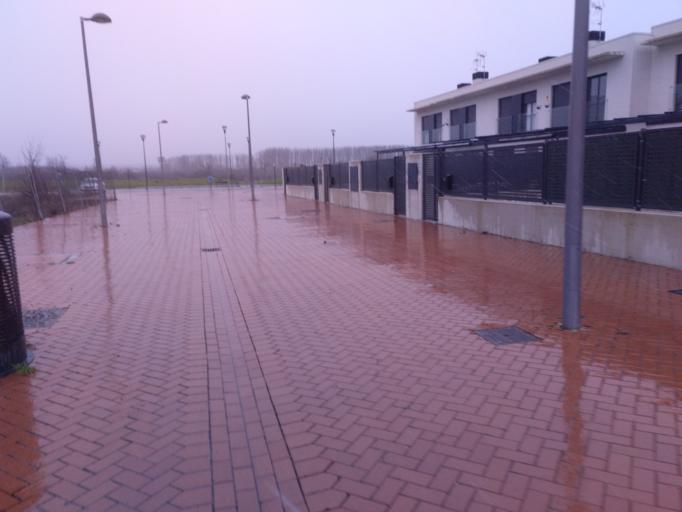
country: ES
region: Basque Country
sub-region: Provincia de Alava
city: Gasteiz / Vitoria
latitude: 42.8510
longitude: -2.6451
